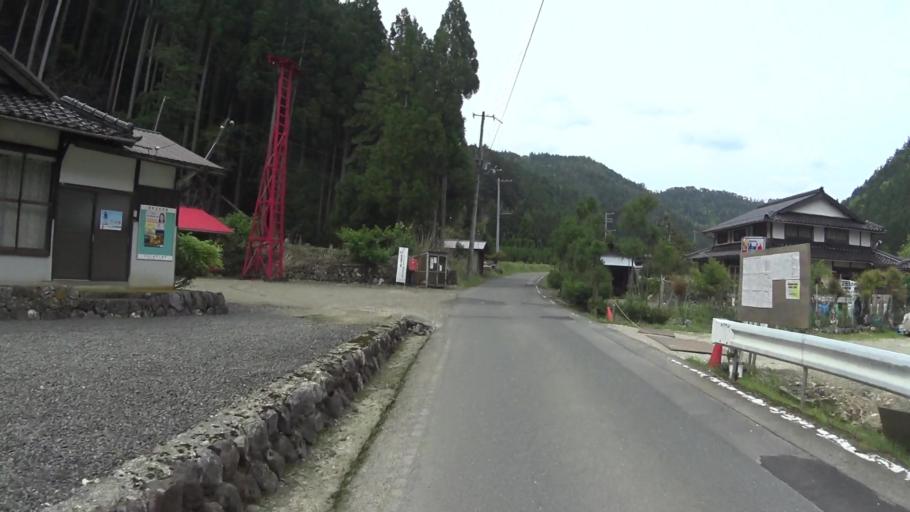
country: JP
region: Kyoto
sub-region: Kyoto-shi
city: Kamigyo-ku
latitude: 35.2118
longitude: 135.7003
